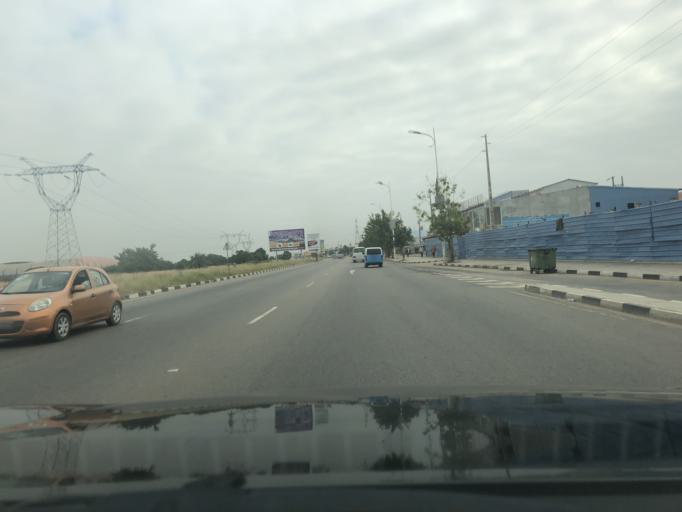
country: AO
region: Luanda
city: Luanda
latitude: -8.9804
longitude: 13.2900
